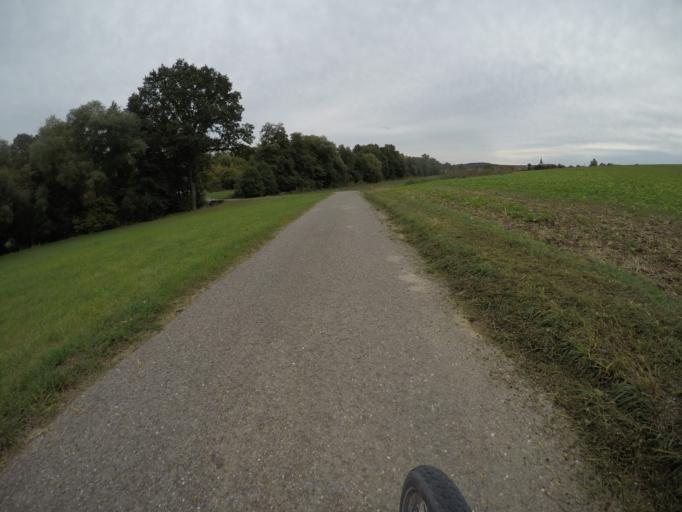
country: DE
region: Baden-Wuerttemberg
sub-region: Karlsruhe Region
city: Muhlacker
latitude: 48.9835
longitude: 8.8564
